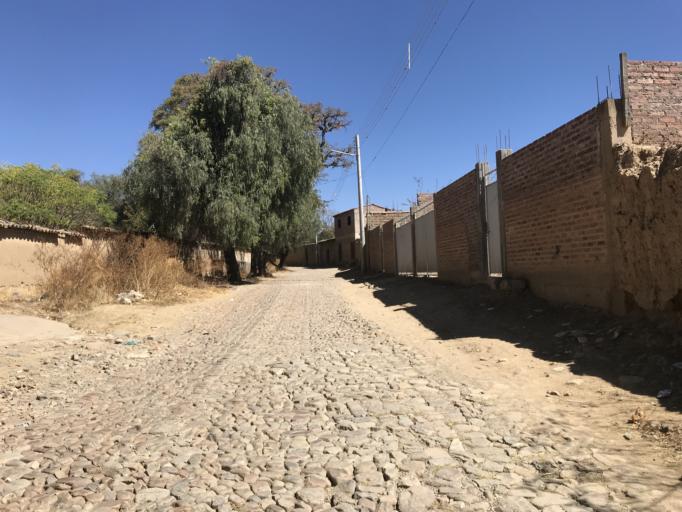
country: BO
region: Cochabamba
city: Tarata
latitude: -17.6162
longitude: -66.0260
